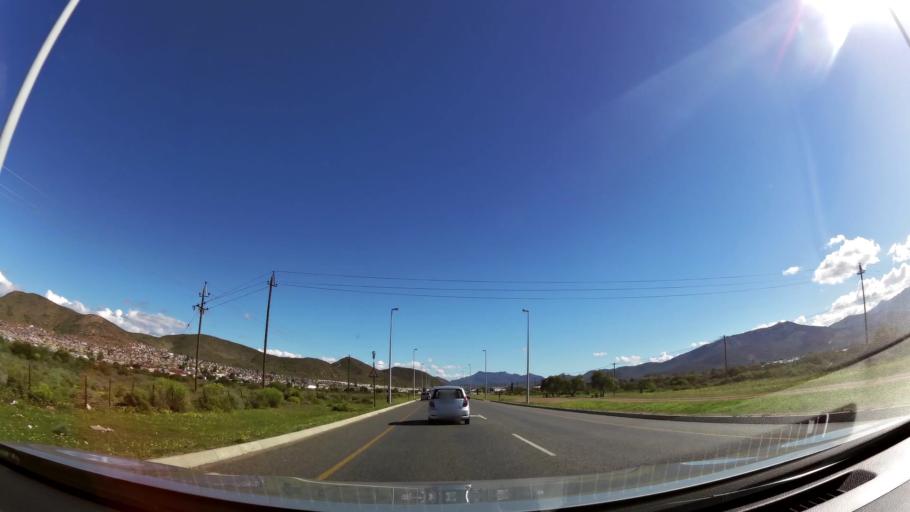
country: ZA
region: Western Cape
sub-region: Cape Winelands District Municipality
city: Ashton
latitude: -33.8148
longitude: 19.9018
